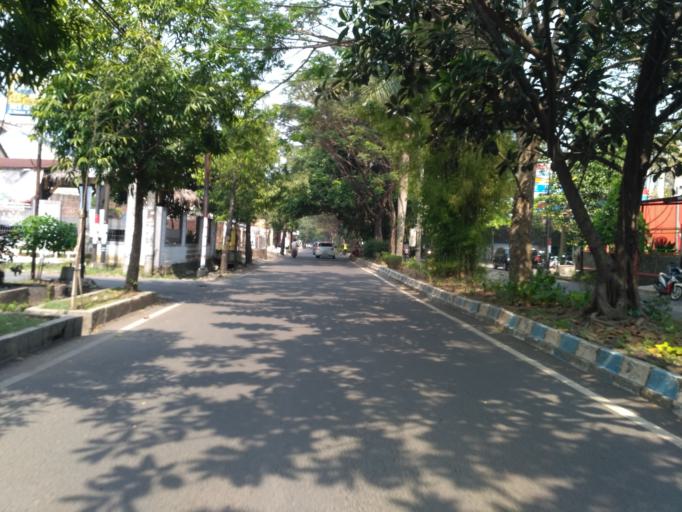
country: ID
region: East Java
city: Malang
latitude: -7.9723
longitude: 112.6636
